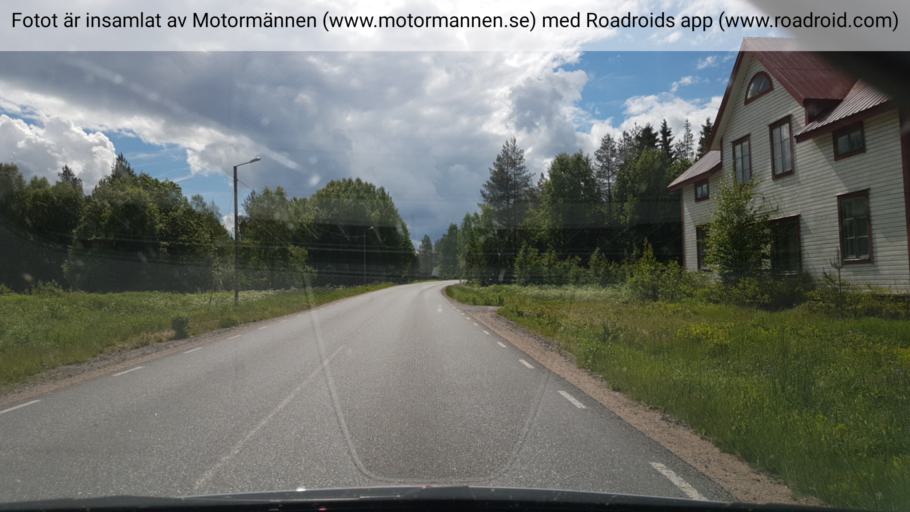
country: FI
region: Lapland
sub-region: Torniolaakso
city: Ylitornio
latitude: 66.2772
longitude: 23.6527
